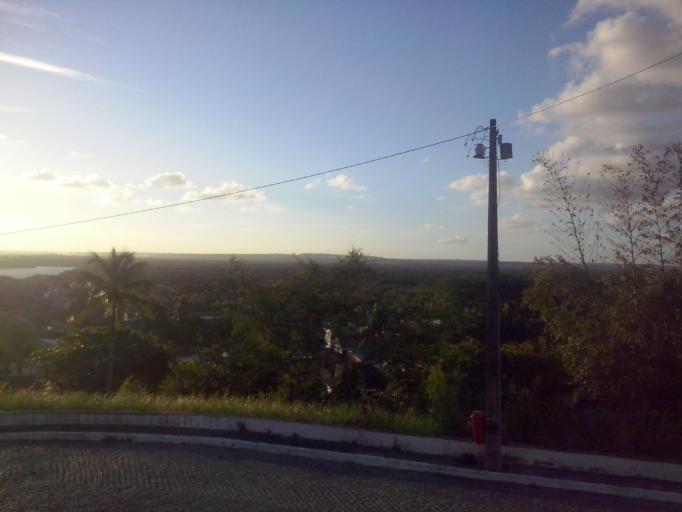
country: BR
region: Paraiba
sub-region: Joao Pessoa
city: Joao Pessoa
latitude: -7.1141
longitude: -34.8847
